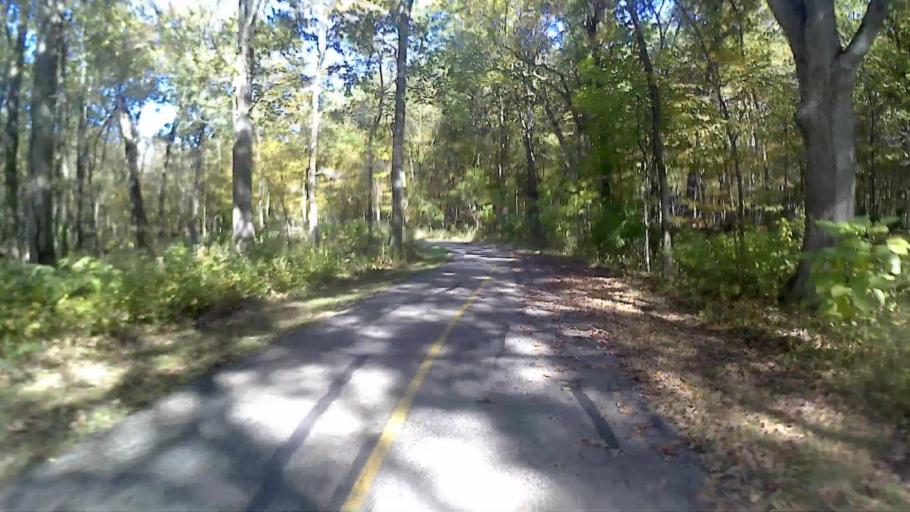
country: US
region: Illinois
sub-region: Cook County
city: Elk Grove Village
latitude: 42.0319
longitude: -88.0028
